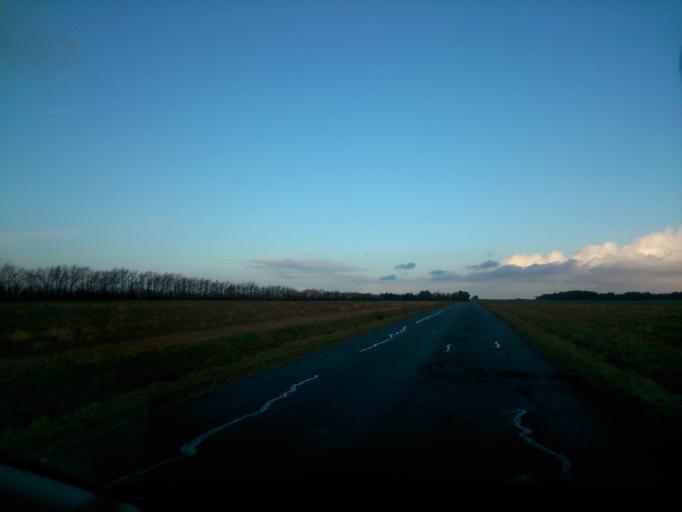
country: DK
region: Central Jutland
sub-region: Ringkobing-Skjern Kommune
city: Videbaek
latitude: 56.0348
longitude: 8.5628
